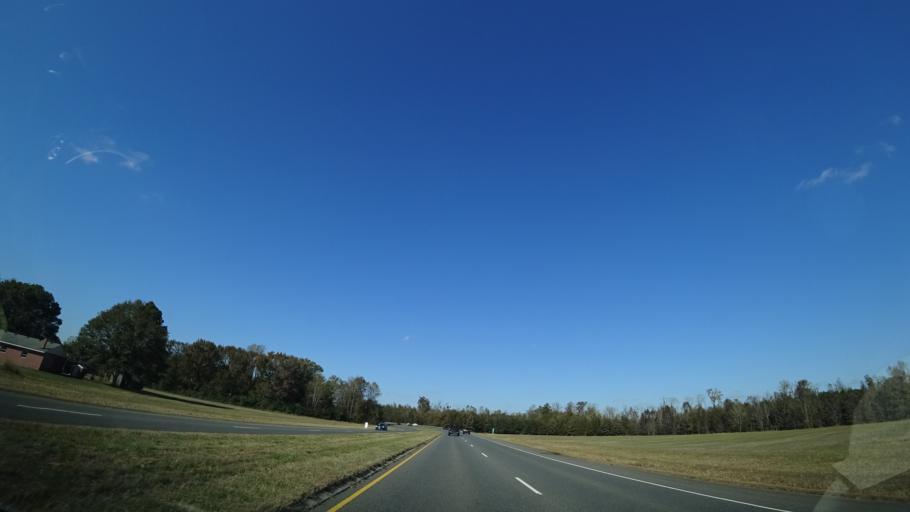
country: US
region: North Carolina
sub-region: Currituck County
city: Moyock
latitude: 36.5580
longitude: -76.1965
